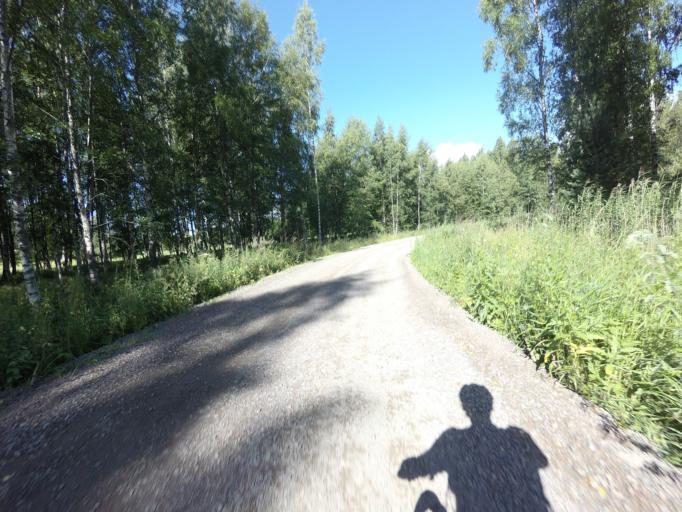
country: FI
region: Uusimaa
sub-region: Helsinki
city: Espoo
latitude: 60.1497
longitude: 24.6103
